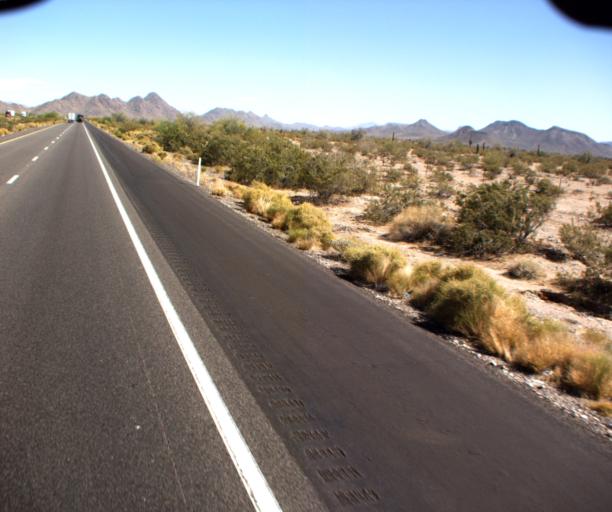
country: US
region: Arizona
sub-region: Maricopa County
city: Gila Bend
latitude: 32.9075
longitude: -112.5908
